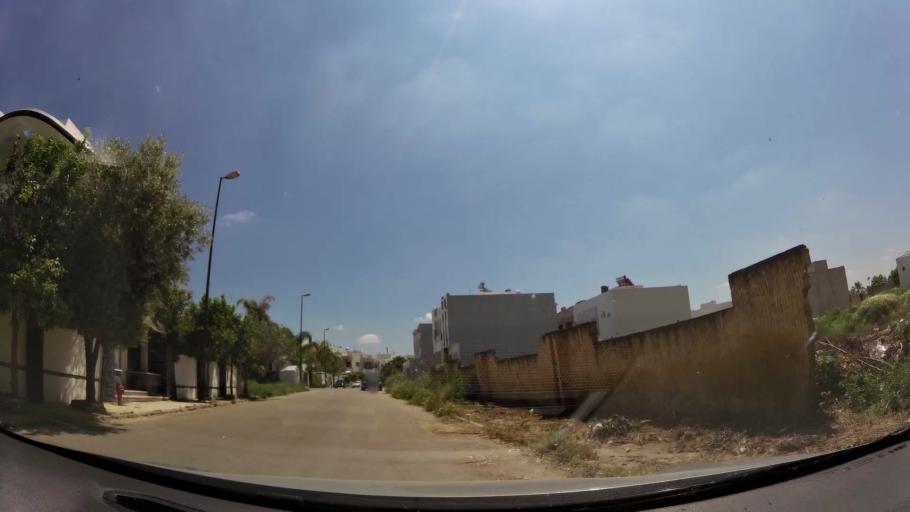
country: MA
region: Fes-Boulemane
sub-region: Fes
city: Fes
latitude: 34.0279
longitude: -5.0139
